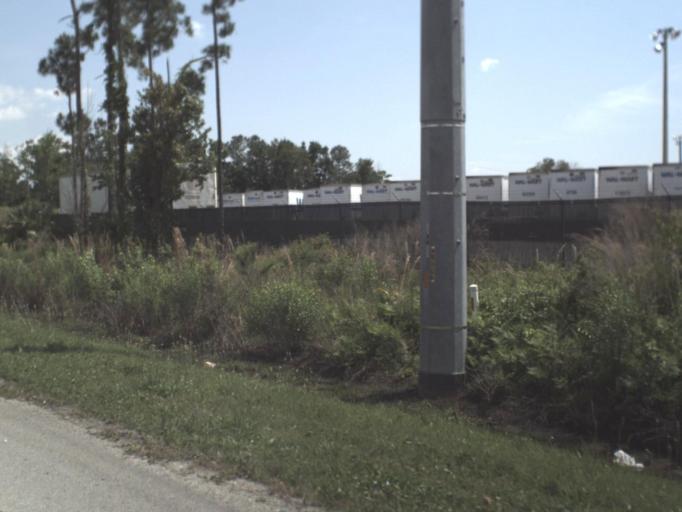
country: US
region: Florida
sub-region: Duval County
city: Jacksonville
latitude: 30.2500
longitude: -81.6053
